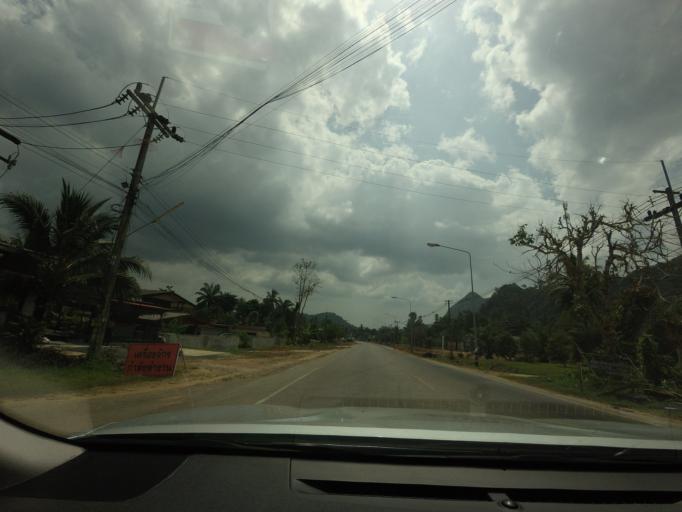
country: TH
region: Phangnga
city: Ban Ao Nang
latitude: 8.1018
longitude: 98.8016
